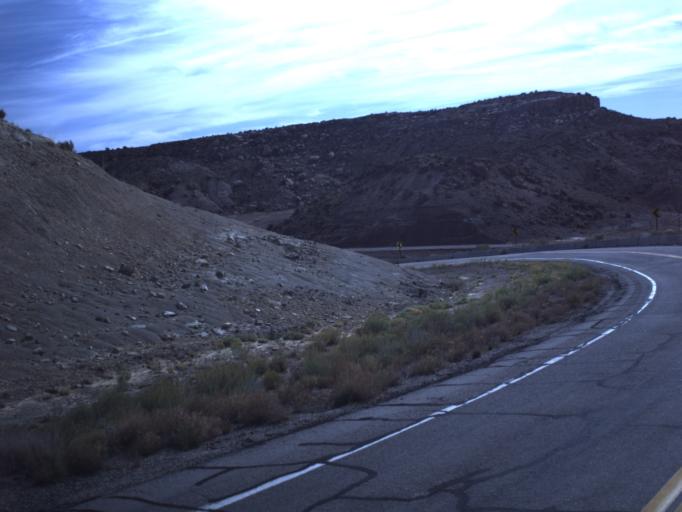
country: US
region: Utah
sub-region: San Juan County
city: Blanding
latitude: 37.3271
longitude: -109.3223
